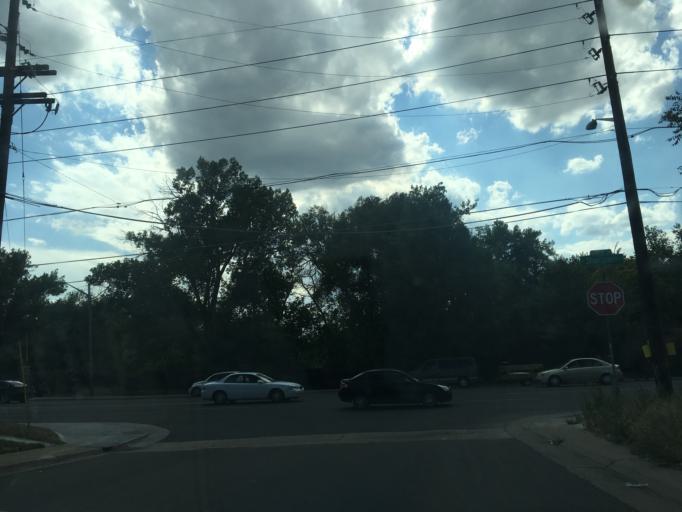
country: US
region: Colorado
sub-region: Jefferson County
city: Lakewood
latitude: 39.6835
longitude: -105.0528
